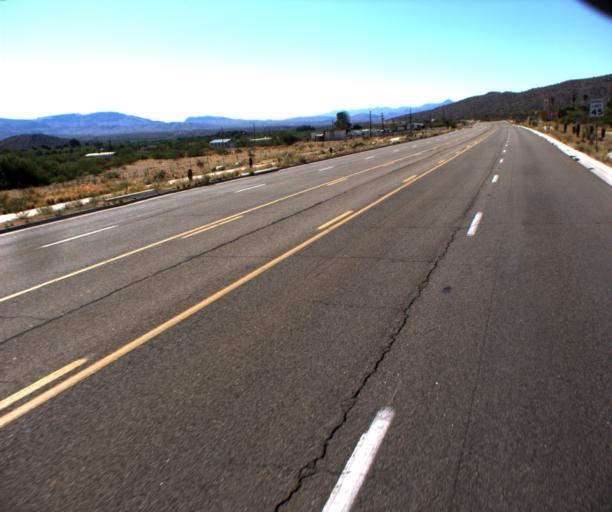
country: US
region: Arizona
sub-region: Yavapai County
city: Bagdad
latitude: 34.7035
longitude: -113.6113
